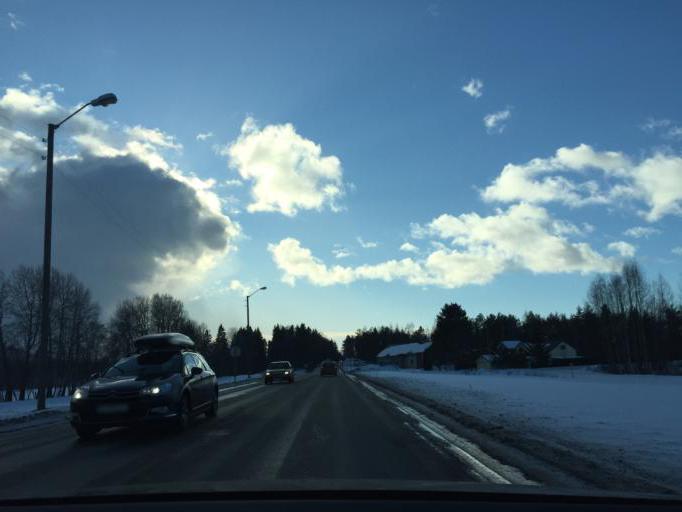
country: NO
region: Hedmark
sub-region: Sor-Odal
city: Skarnes
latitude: 60.2520
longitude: 11.6714
